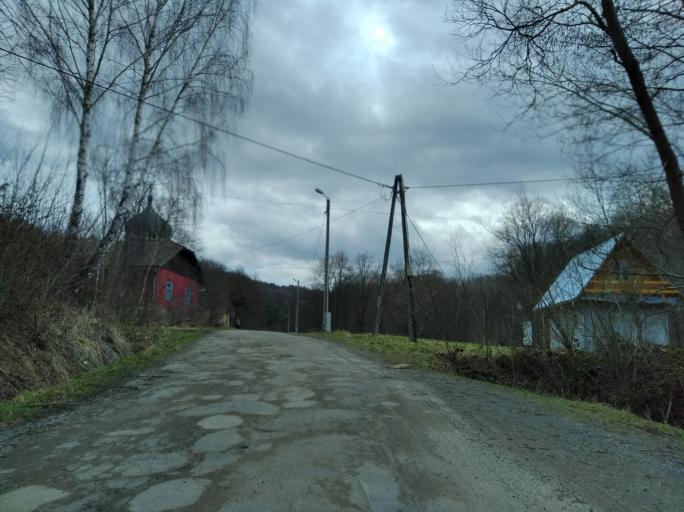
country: PL
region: Subcarpathian Voivodeship
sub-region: Powiat strzyzowski
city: Wysoka Strzyzowska
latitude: 49.7904
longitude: 21.7254
